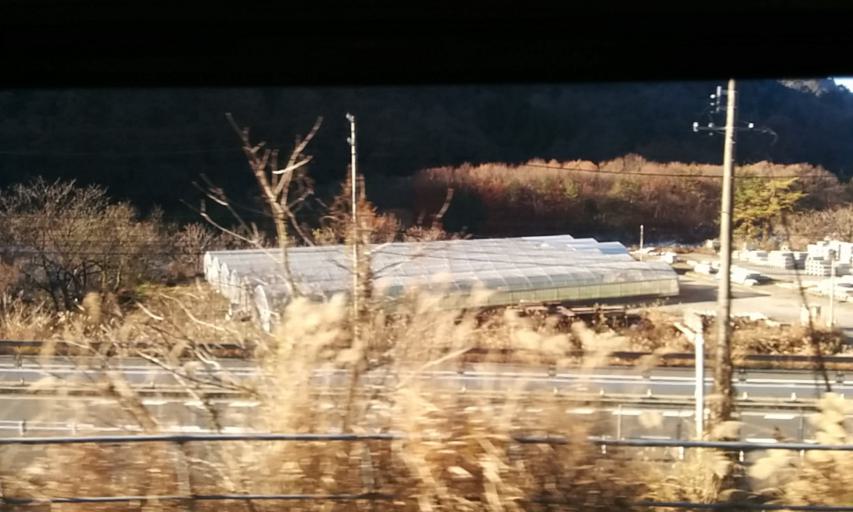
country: JP
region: Nagano
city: Iida
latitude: 35.7339
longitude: 137.7157
